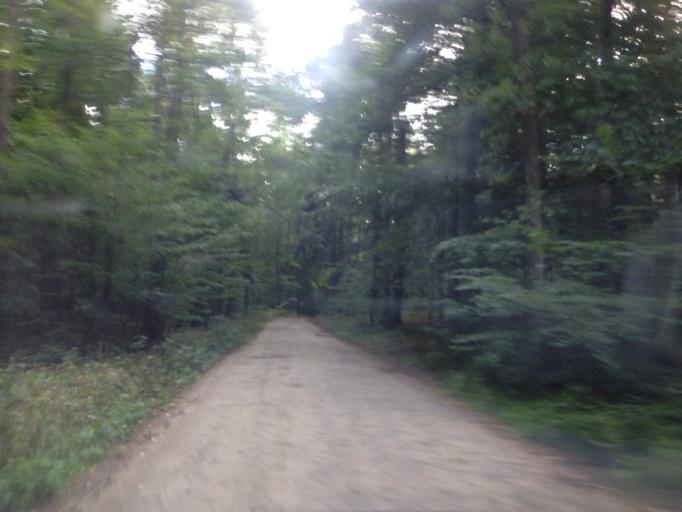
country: PL
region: Warmian-Masurian Voivodeship
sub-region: Powiat ilawski
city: Susz
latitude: 53.7620
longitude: 19.3125
